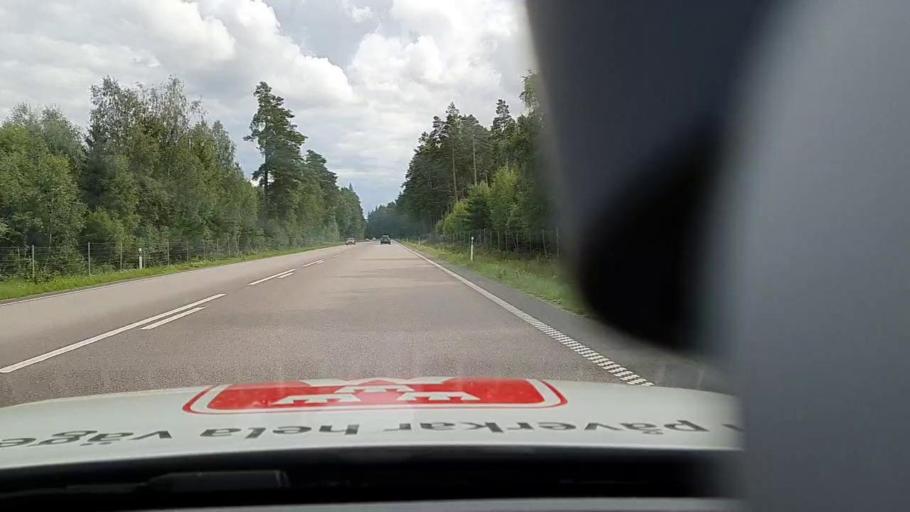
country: SE
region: Vaestra Goetaland
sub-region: Lidkopings Kommun
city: Lidkoping
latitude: 58.4731
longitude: 13.2089
